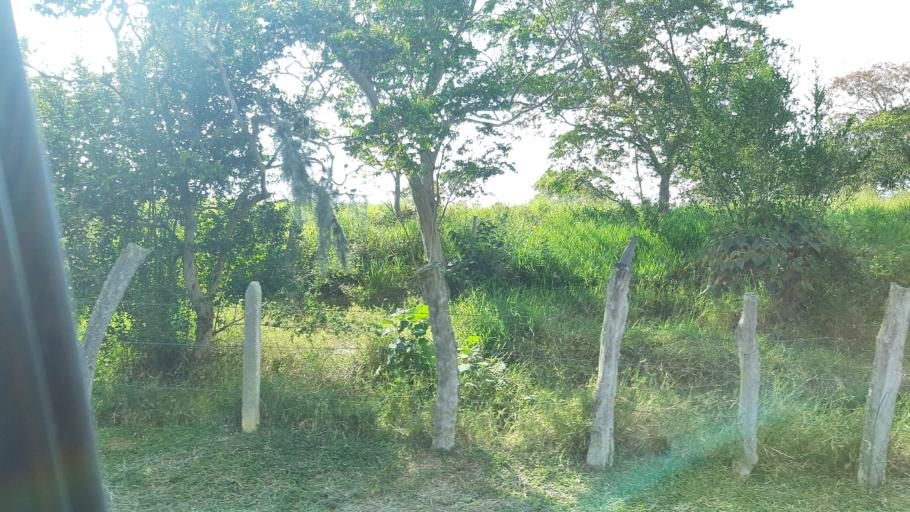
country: CO
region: Boyaca
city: Moniquira
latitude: 5.8163
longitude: -73.5995
